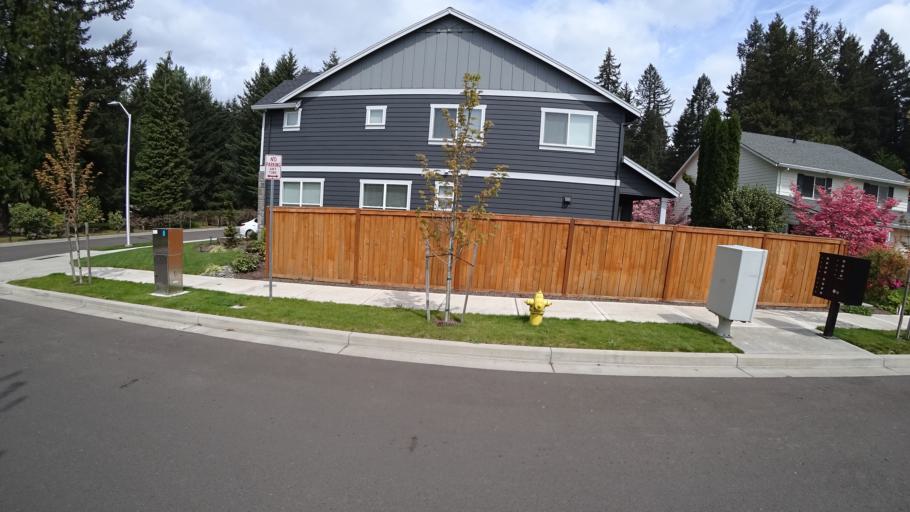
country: US
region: Oregon
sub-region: Washington County
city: Hillsboro
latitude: 45.5486
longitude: -122.9979
